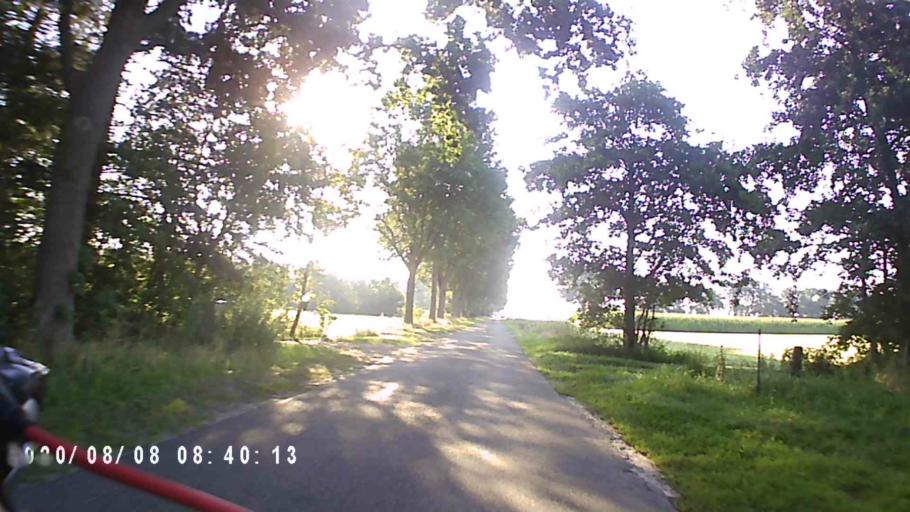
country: NL
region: Groningen
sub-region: Gemeente Leek
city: Leek
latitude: 53.0695
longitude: 6.3585
